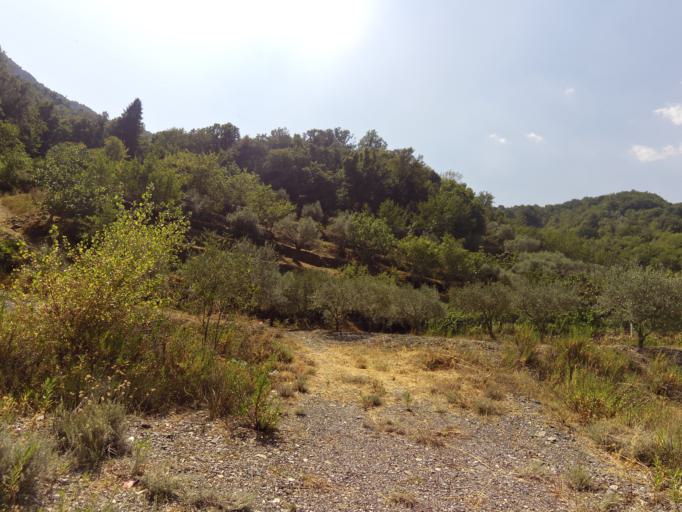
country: IT
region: Calabria
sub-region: Provincia di Reggio Calabria
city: Pazzano
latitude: 38.4741
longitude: 16.4364
